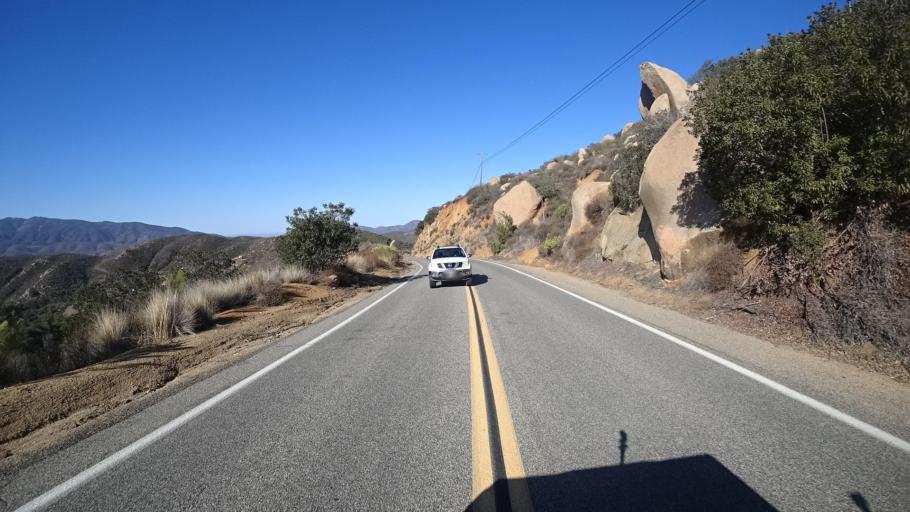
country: US
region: California
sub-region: San Diego County
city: Jamul
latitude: 32.6728
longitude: -116.7674
